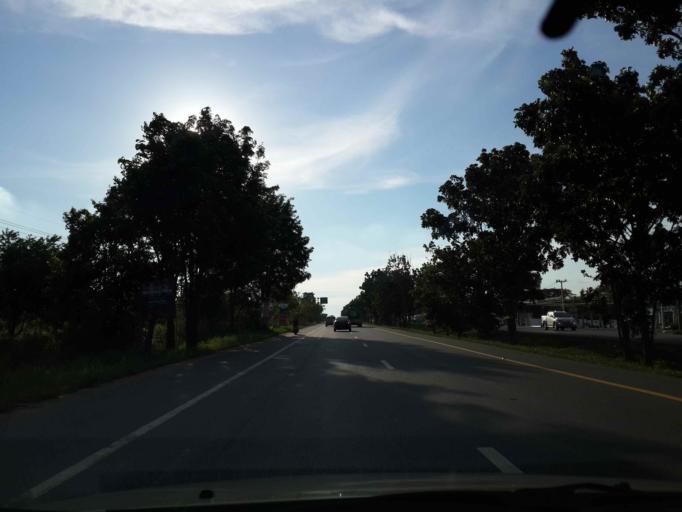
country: TH
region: Chon Buri
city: Bang Lamung
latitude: 12.9812
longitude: 100.9558
